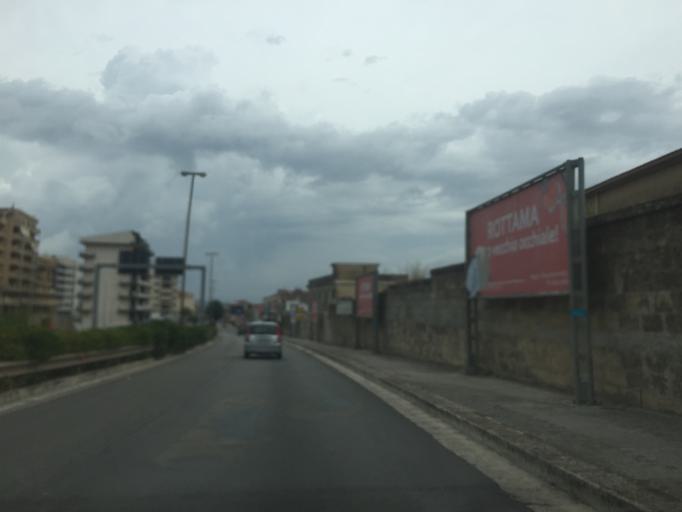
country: IT
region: Sicily
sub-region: Ragusa
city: Ragusa
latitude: 36.9071
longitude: 14.7220
